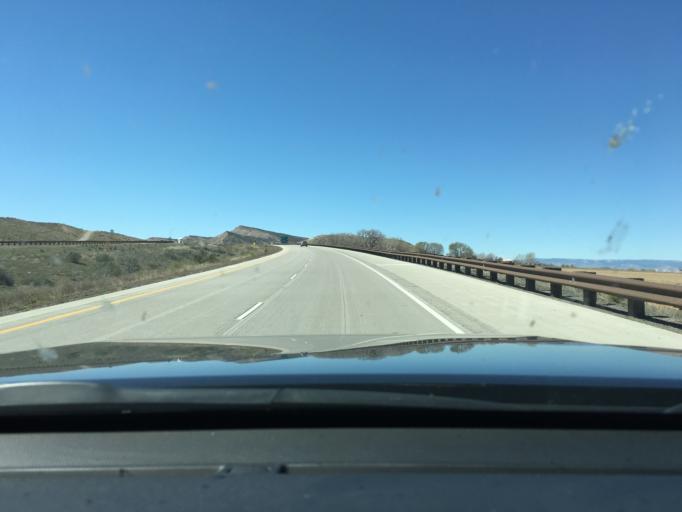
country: US
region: Colorado
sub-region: Mesa County
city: Loma
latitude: 39.1773
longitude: -108.8040
